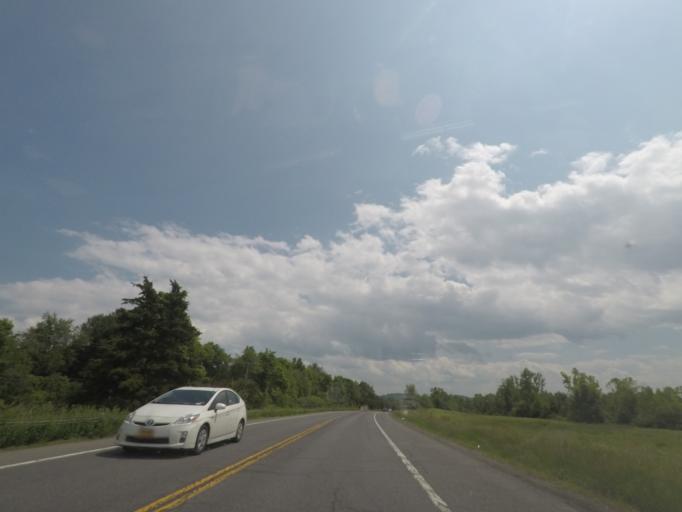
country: US
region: New York
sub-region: Columbia County
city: Oakdale
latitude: 42.1589
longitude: -73.7467
